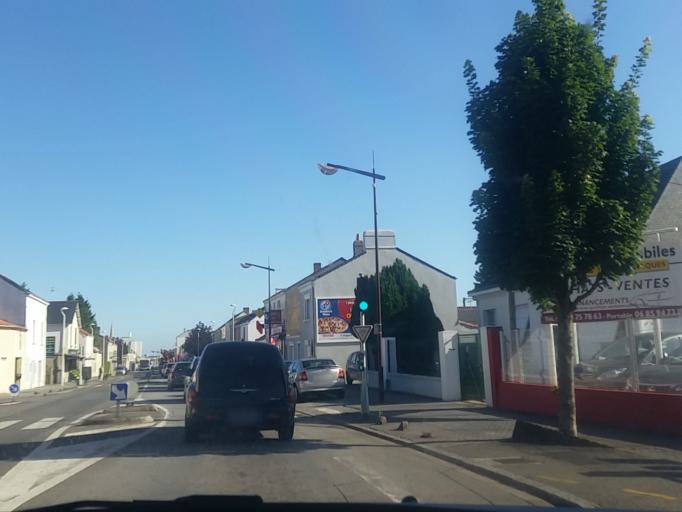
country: FR
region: Pays de la Loire
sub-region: Departement de la Loire-Atlantique
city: Reze
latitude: 47.1767
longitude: -1.5438
